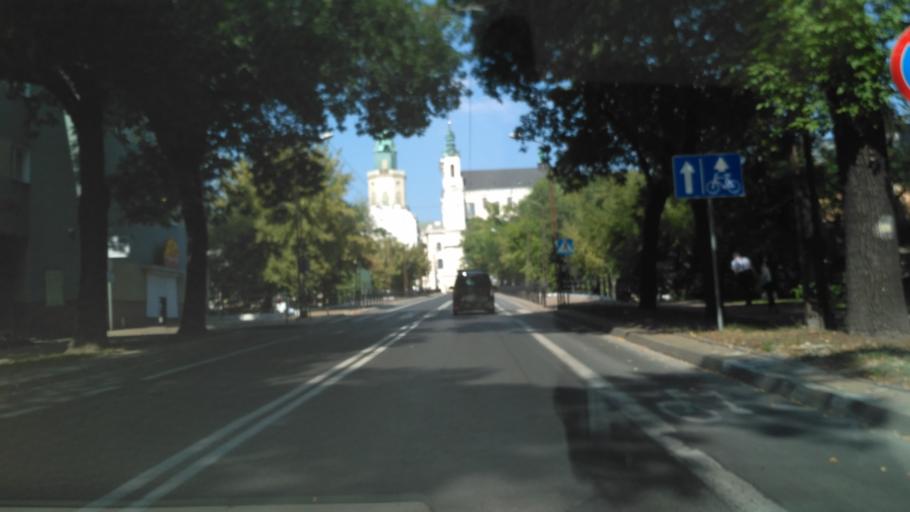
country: PL
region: Lublin Voivodeship
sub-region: Powiat lubelski
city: Lublin
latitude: 51.2445
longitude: 22.5687
